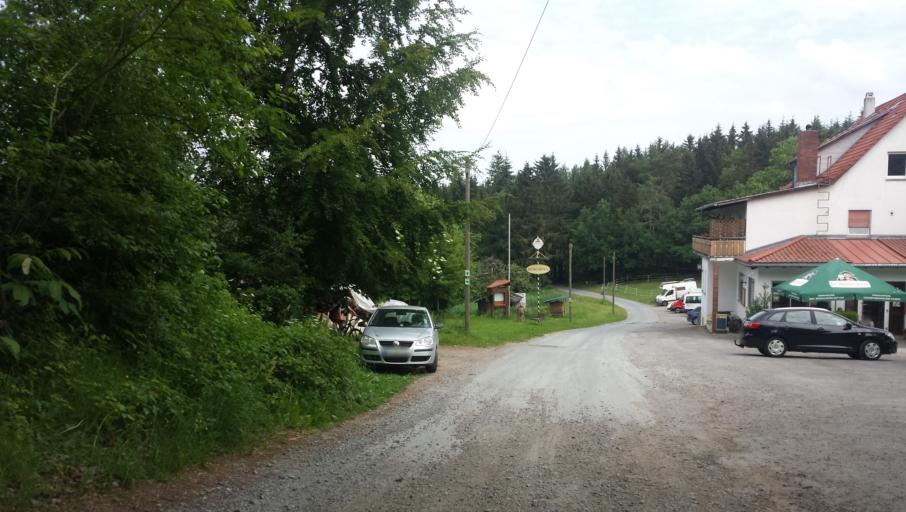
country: DE
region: Hesse
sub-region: Regierungsbezirk Darmstadt
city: Furth
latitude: 49.6236
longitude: 8.8109
